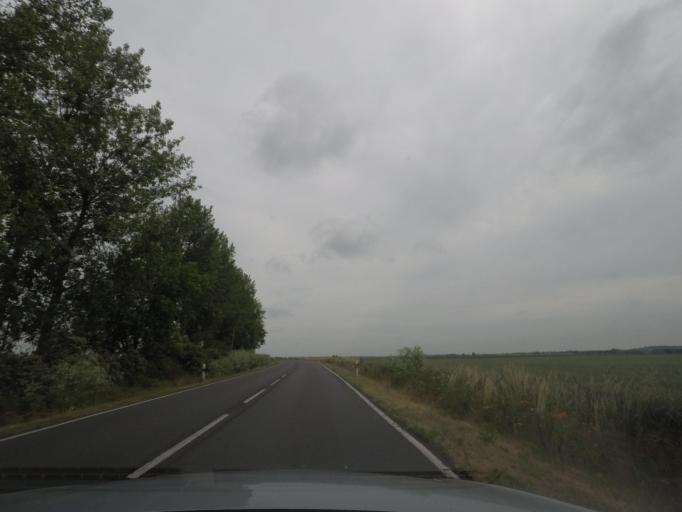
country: DE
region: Saxony-Anhalt
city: Wanzleben
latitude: 52.0416
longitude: 11.4094
